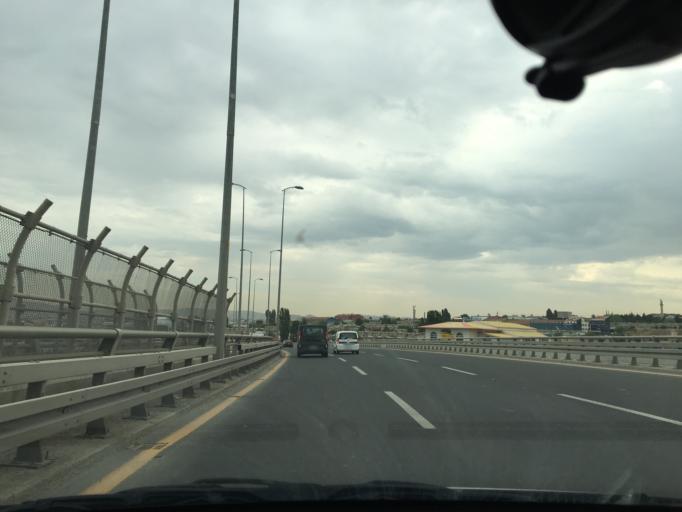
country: TR
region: Ankara
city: Batikent
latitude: 39.9280
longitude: 32.7106
